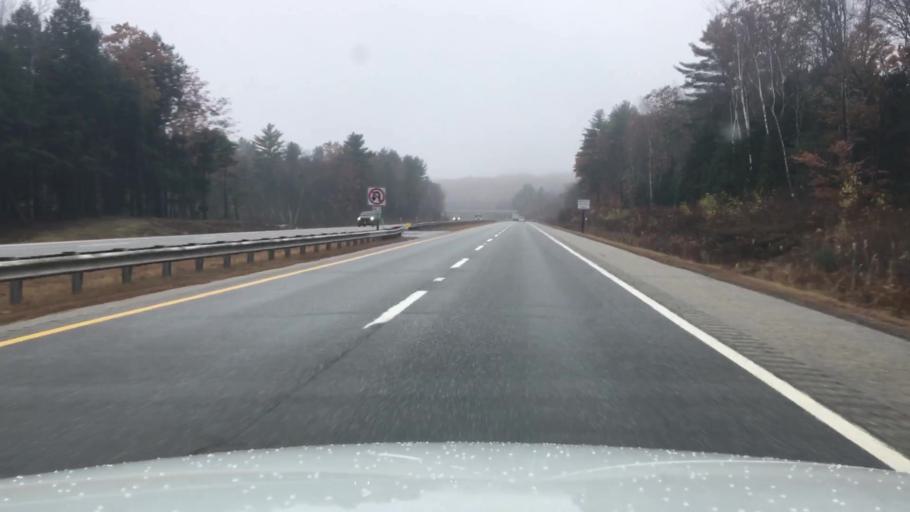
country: US
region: Maine
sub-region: Androscoggin County
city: Sabattus
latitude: 44.1244
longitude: -70.0282
